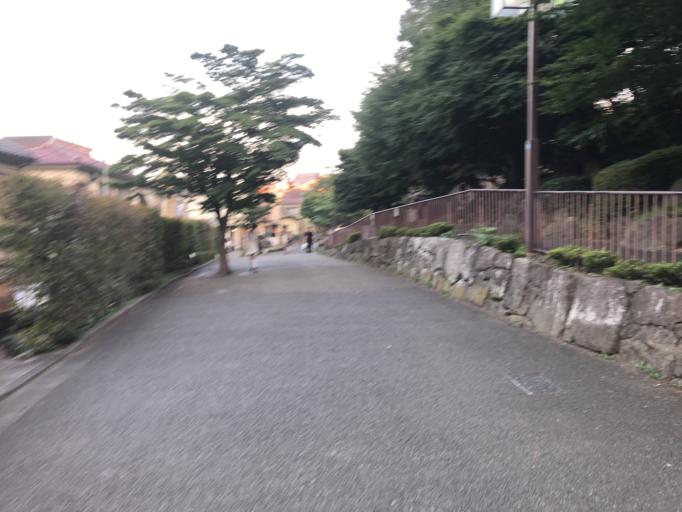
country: JP
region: Tokyo
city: Tokyo
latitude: 35.6240
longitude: 139.7045
